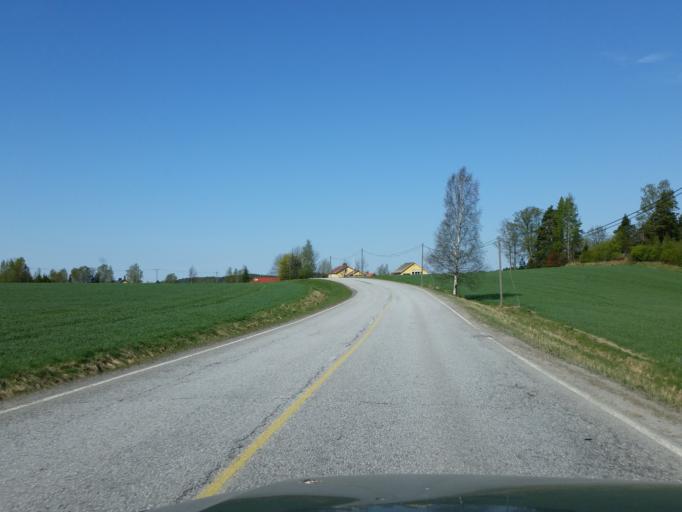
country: FI
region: Uusimaa
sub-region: Helsinki
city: Lohja
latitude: 60.1772
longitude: 24.0844
